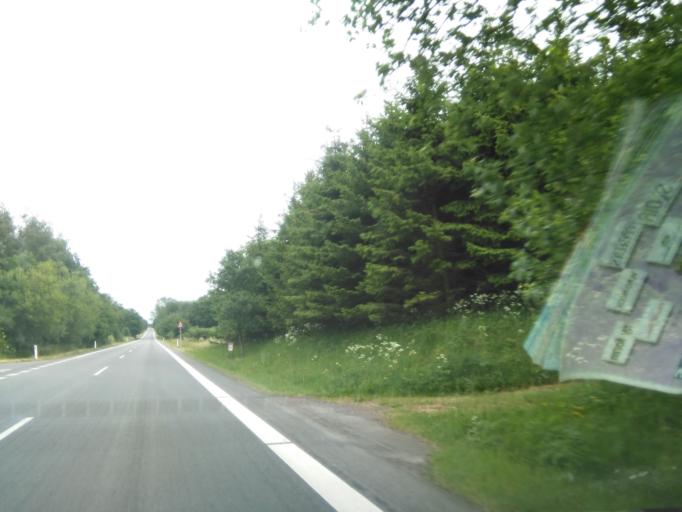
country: DK
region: Capital Region
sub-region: Bornholm Kommune
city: Akirkeby
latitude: 55.1179
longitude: 14.8362
